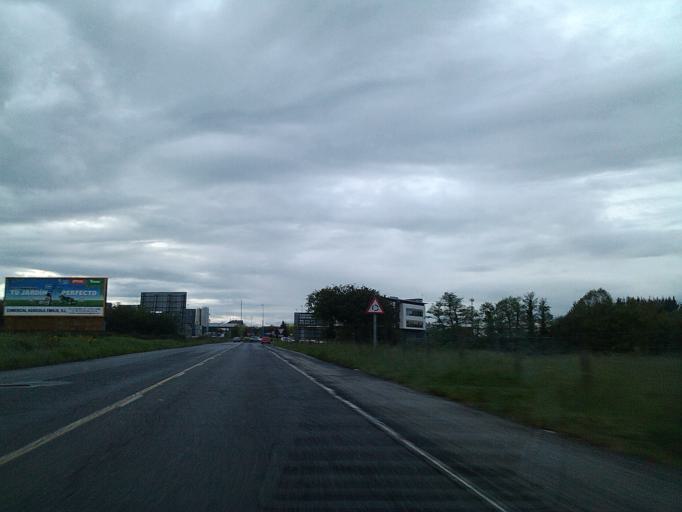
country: ES
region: Galicia
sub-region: Provincia de Lugo
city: Lugo
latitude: 43.0414
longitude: -7.5685
